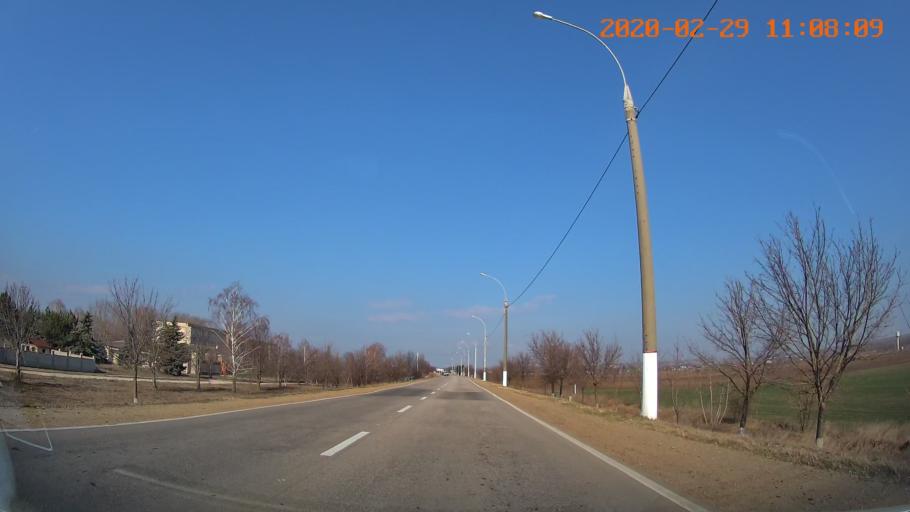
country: MD
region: Criuleni
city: Criuleni
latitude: 47.2314
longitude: 29.1776
